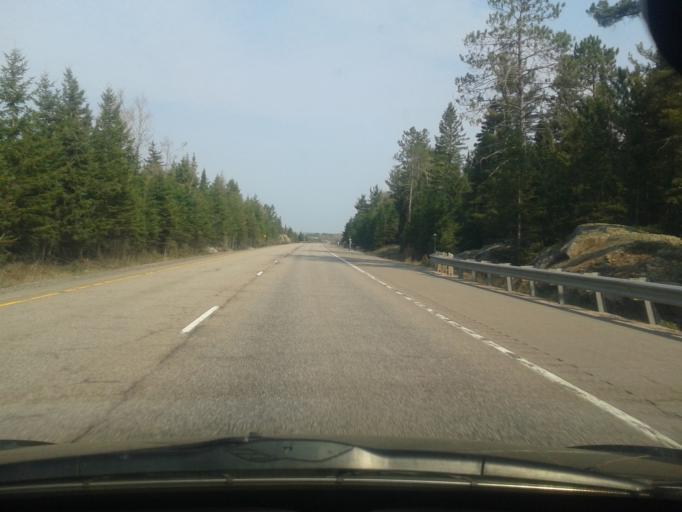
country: CA
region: Ontario
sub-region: Nipissing District
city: North Bay
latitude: 46.2539
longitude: -79.3761
